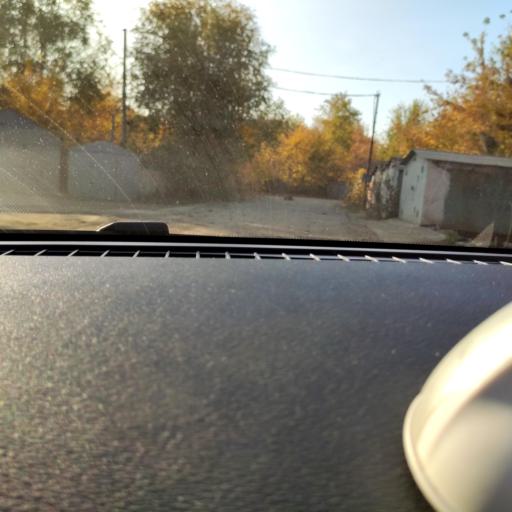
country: RU
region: Samara
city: Samara
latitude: 53.2017
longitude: 50.2392
